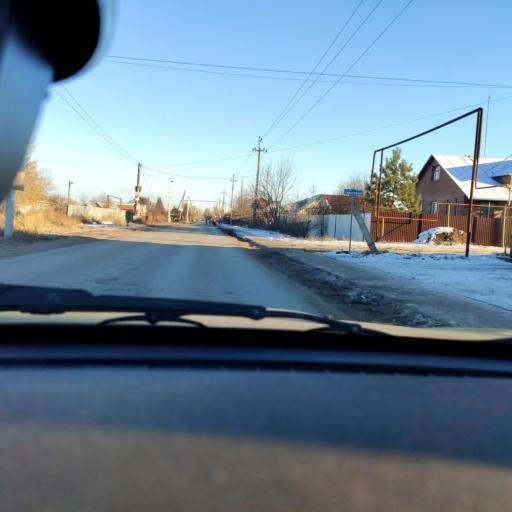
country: RU
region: Samara
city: Tol'yatti
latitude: 53.5559
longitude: 49.3954
